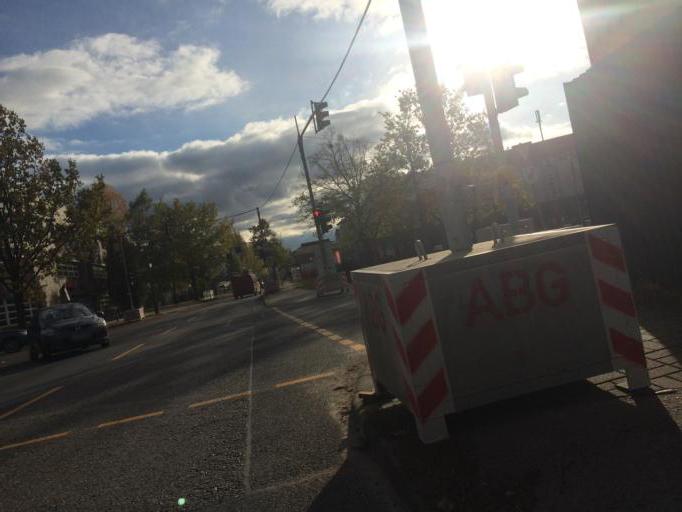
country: DE
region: Berlin
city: Buchholz
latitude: 52.6129
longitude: 13.4314
